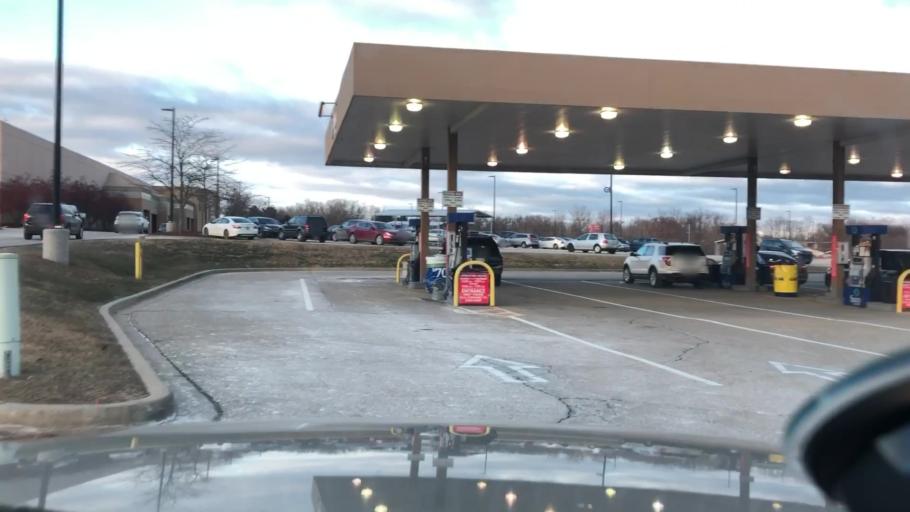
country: US
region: Michigan
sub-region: Jackson County
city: Jackson
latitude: 42.2665
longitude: -84.4609
